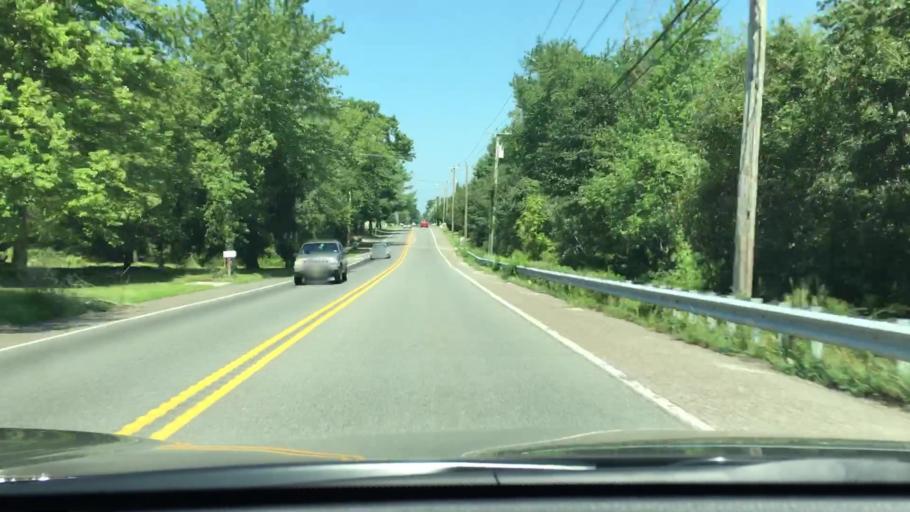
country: US
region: New Jersey
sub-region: Cumberland County
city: Laurel Lake
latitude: 39.3160
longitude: -75.0108
